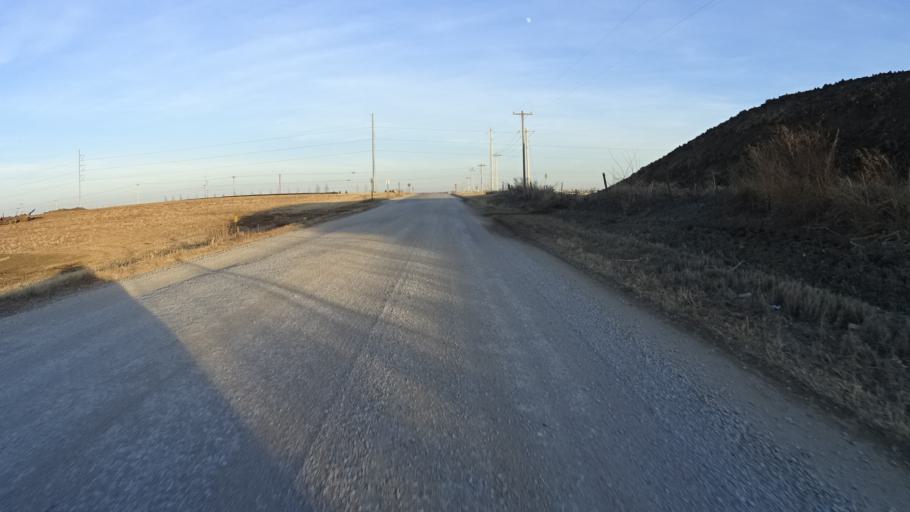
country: US
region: Nebraska
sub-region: Sarpy County
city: Papillion
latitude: 41.1326
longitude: -96.0935
